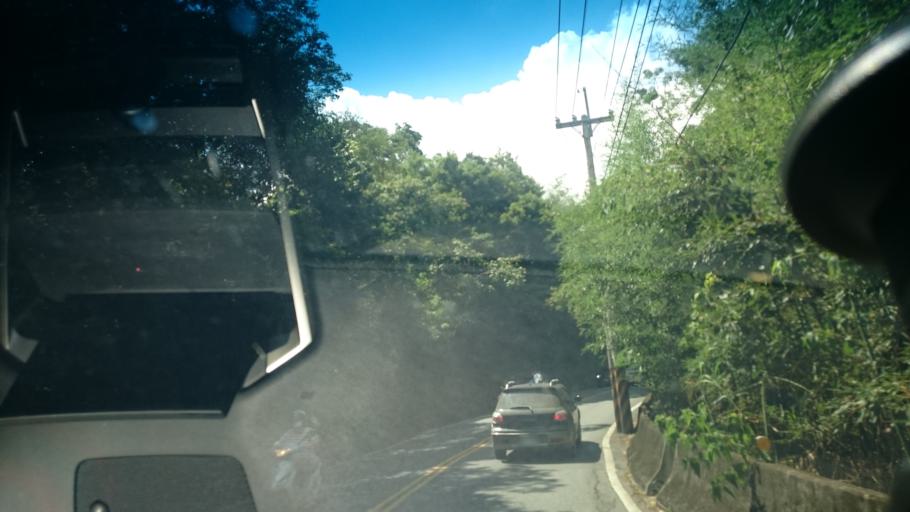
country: TW
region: Taiwan
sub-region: Nantou
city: Puli
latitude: 24.0276
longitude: 121.1438
